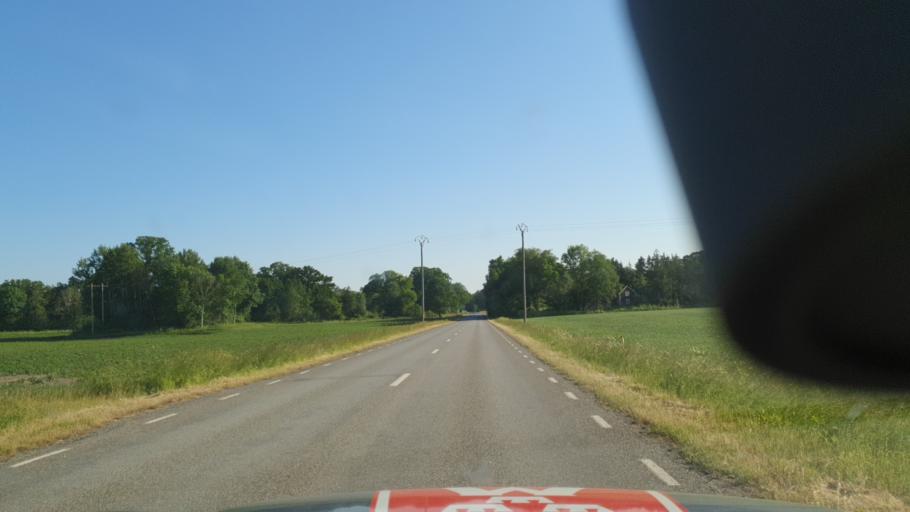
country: SE
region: Kalmar
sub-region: Kalmar Kommun
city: Ljungbyholm
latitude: 56.5045
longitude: 16.1448
